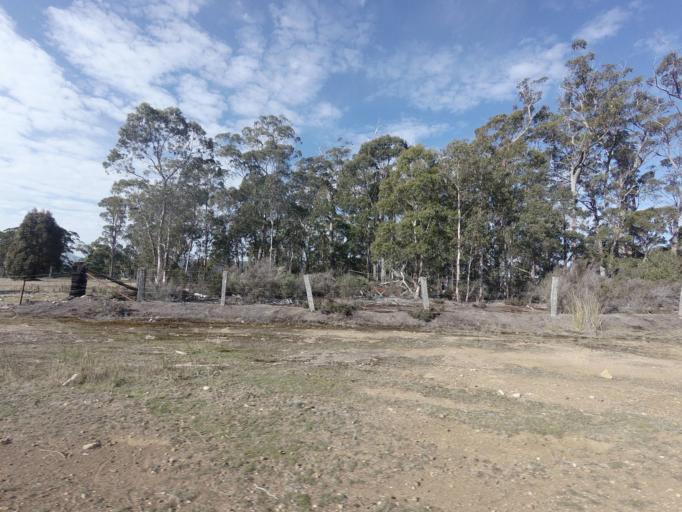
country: AU
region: Tasmania
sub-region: Sorell
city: Sorell
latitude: -42.5025
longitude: 147.4790
